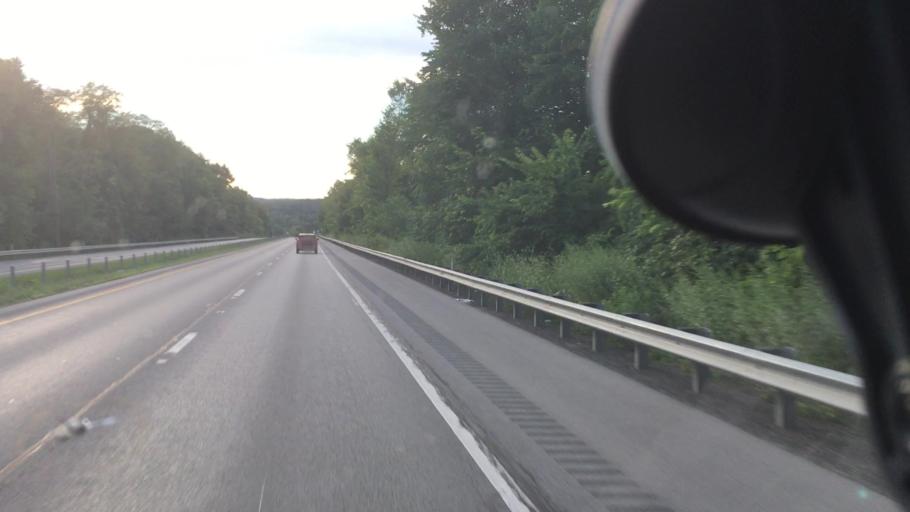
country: US
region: Pennsylvania
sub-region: Beaver County
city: Big Beaver
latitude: 40.7881
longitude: -80.4046
